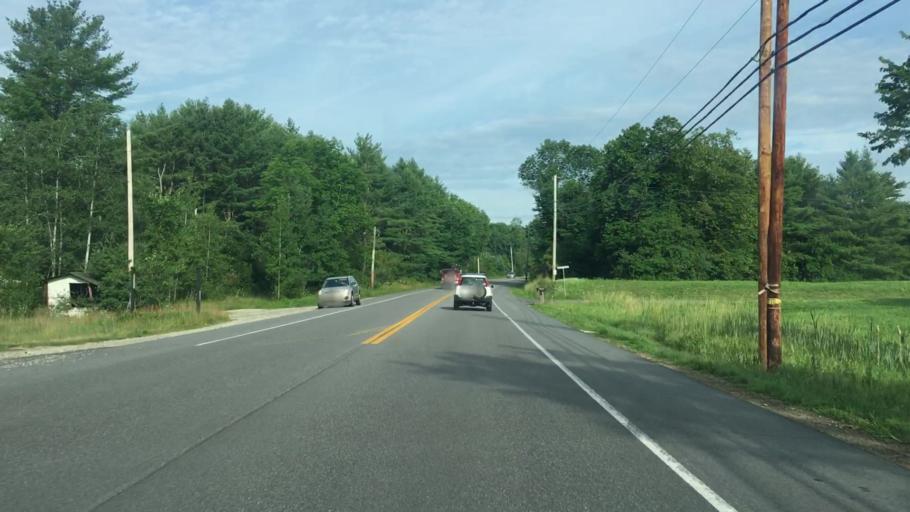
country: US
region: Maine
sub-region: Cumberland County
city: Gorham
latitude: 43.6851
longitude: -70.4787
